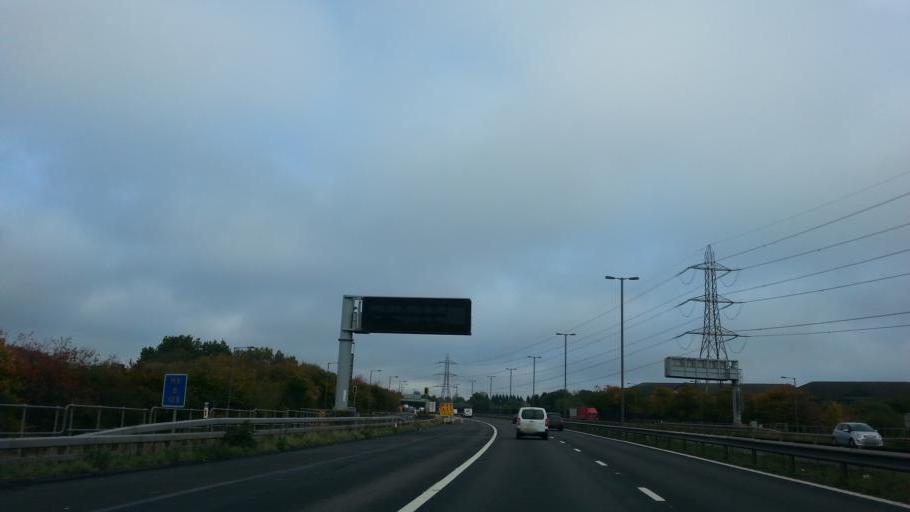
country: GB
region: England
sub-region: City and Borough of Birmingham
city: Bartley Green
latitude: 52.4512
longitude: -2.0133
